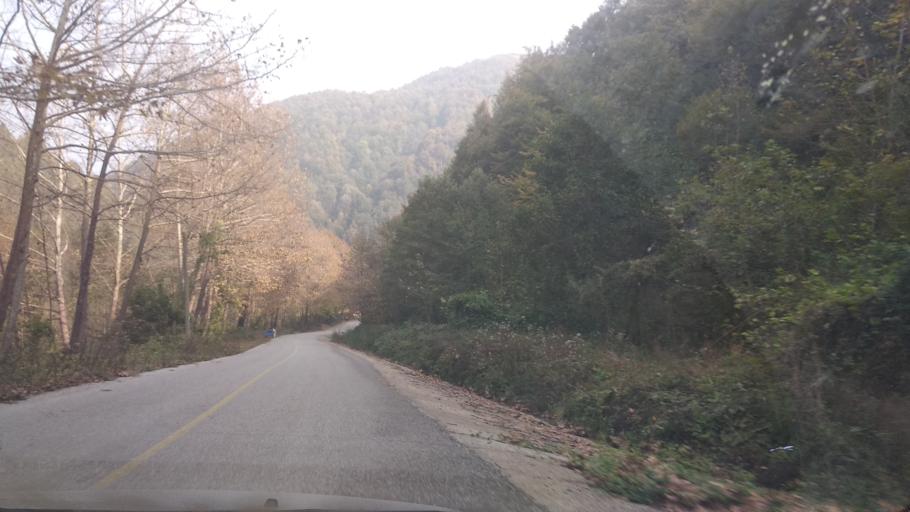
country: TR
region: Duzce
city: Kaynasli
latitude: 40.7268
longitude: 31.2570
